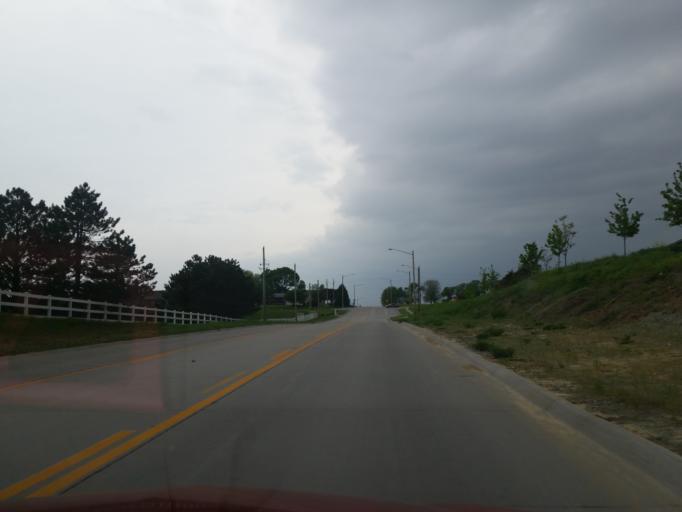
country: US
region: Nebraska
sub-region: Douglas County
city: Bennington
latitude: 41.3212
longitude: -96.1330
